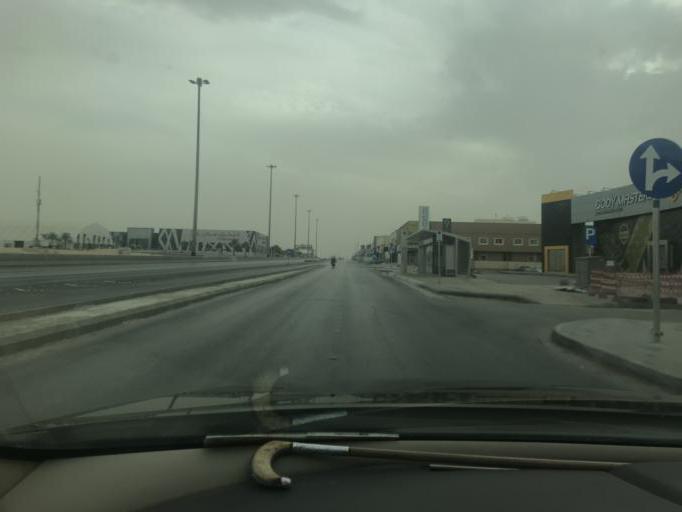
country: SA
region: Ar Riyad
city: Riyadh
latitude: 24.7718
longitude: 46.7195
